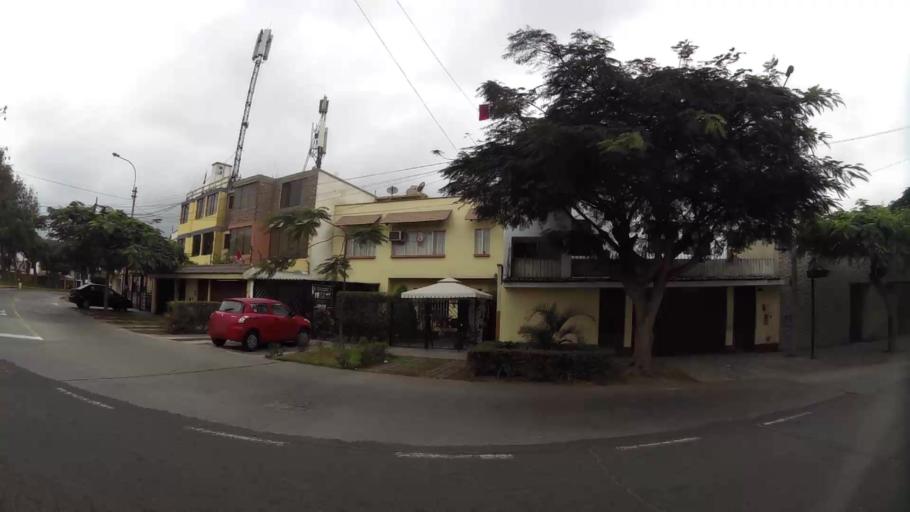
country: PE
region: Lima
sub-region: Lima
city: Surco
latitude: -12.1445
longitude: -76.9919
